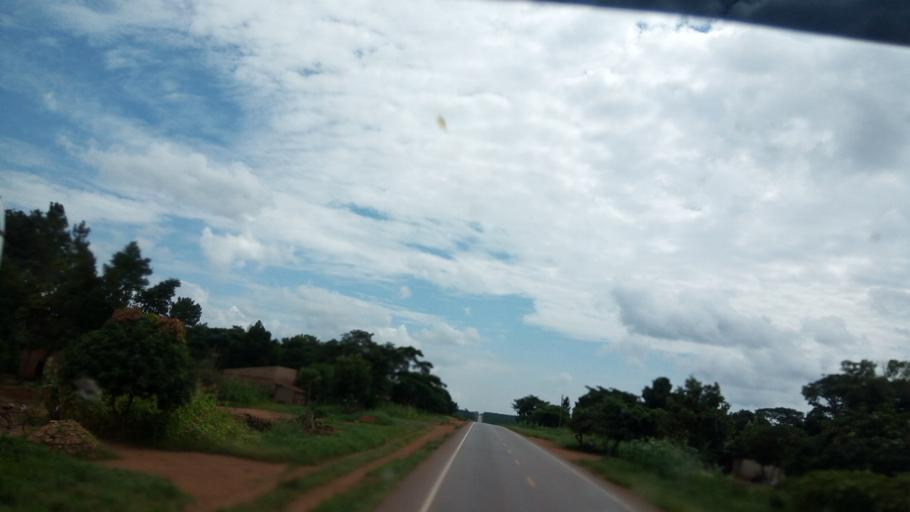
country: UG
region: Central Region
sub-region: Nakasongola District
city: Nakasongola
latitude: 1.1232
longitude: 32.4655
